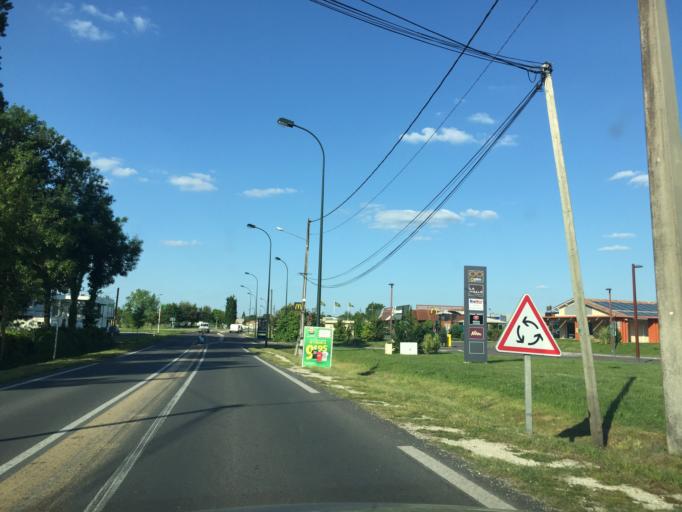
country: FR
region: Aquitaine
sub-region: Departement de la Gironde
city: Les Peintures
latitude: 45.0517
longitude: -0.1138
